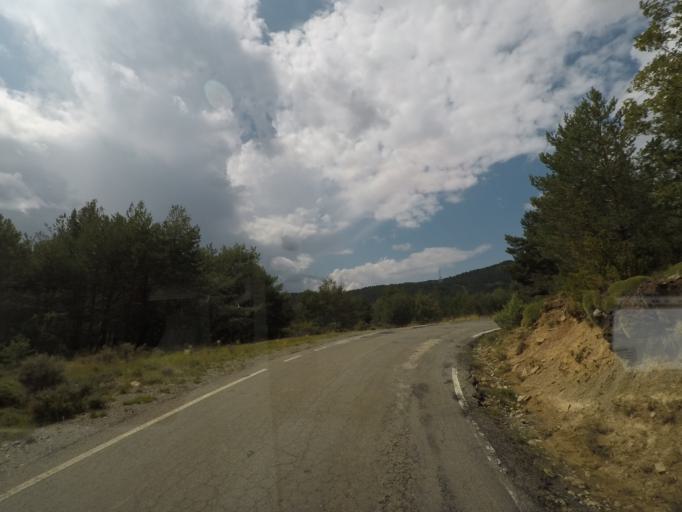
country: ES
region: Aragon
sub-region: Provincia de Huesca
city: Boltana
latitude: 42.4026
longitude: -0.0144
